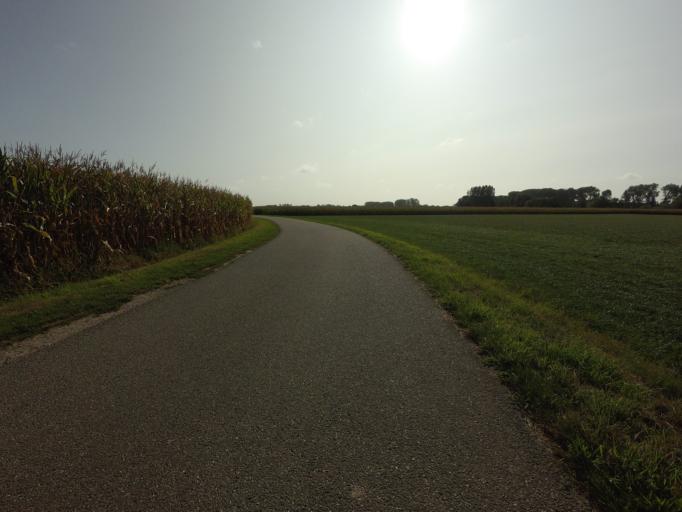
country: NL
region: Limburg
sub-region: Gemeente Roerdalen
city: Melick
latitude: 51.1526
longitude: 6.0225
